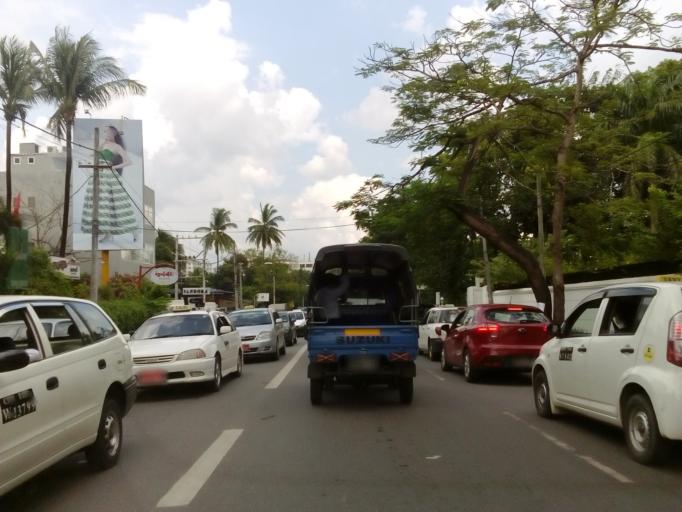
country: MM
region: Yangon
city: Yangon
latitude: 16.8186
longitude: 96.1588
